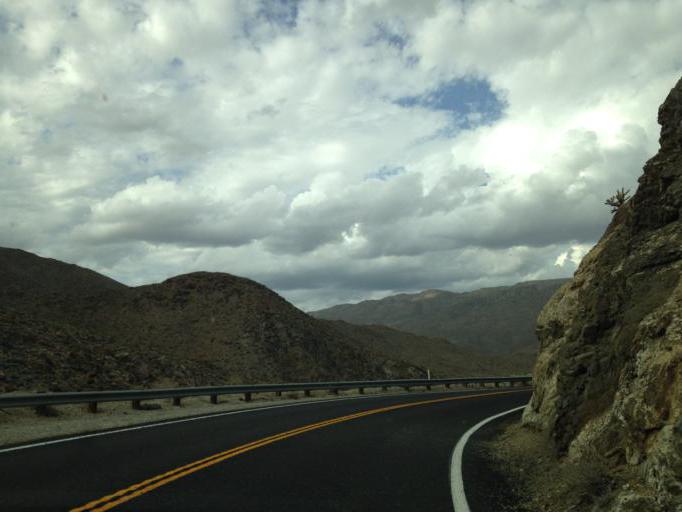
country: US
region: California
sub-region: San Diego County
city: Borrego Springs
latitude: 33.1221
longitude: -116.4356
